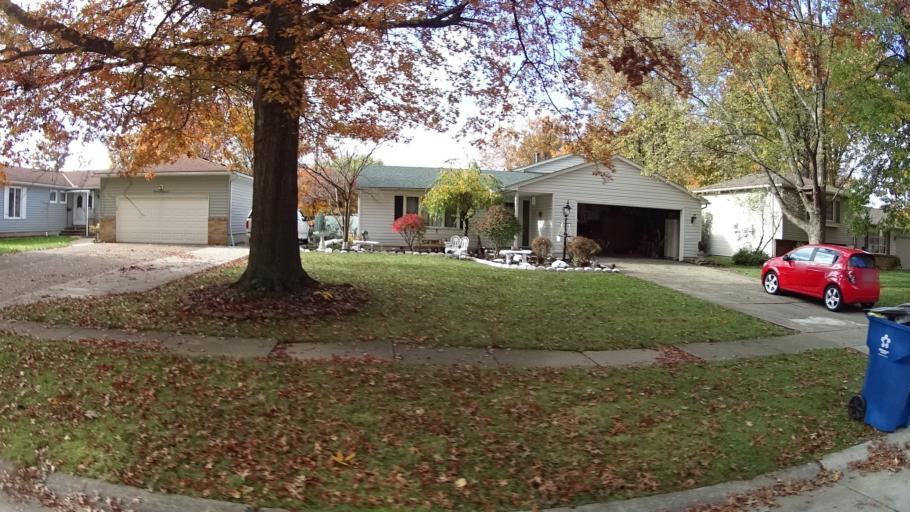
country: US
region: Ohio
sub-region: Lorain County
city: Lorain
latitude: 41.4244
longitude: -82.1992
